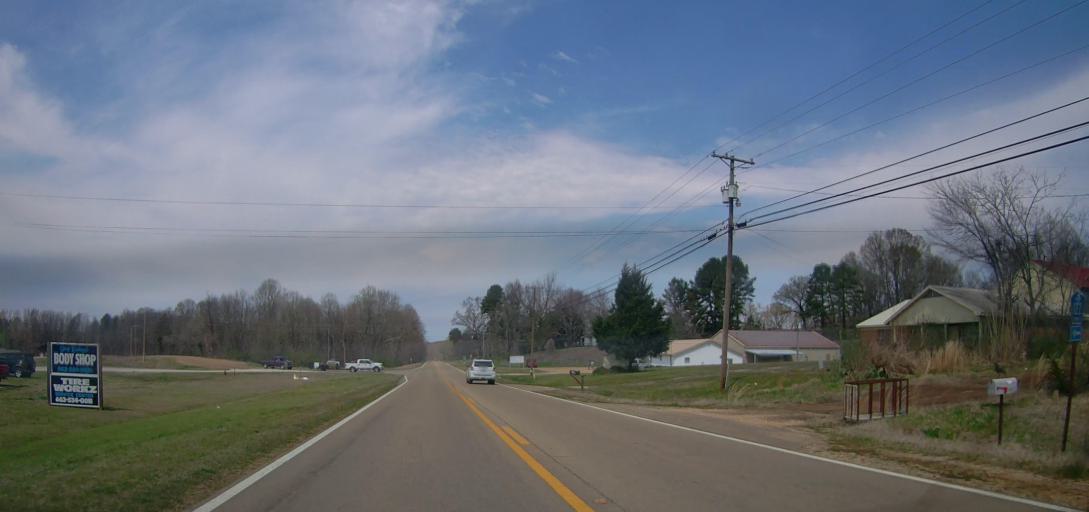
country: US
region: Mississippi
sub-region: Union County
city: New Albany
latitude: 34.4581
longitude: -88.9769
